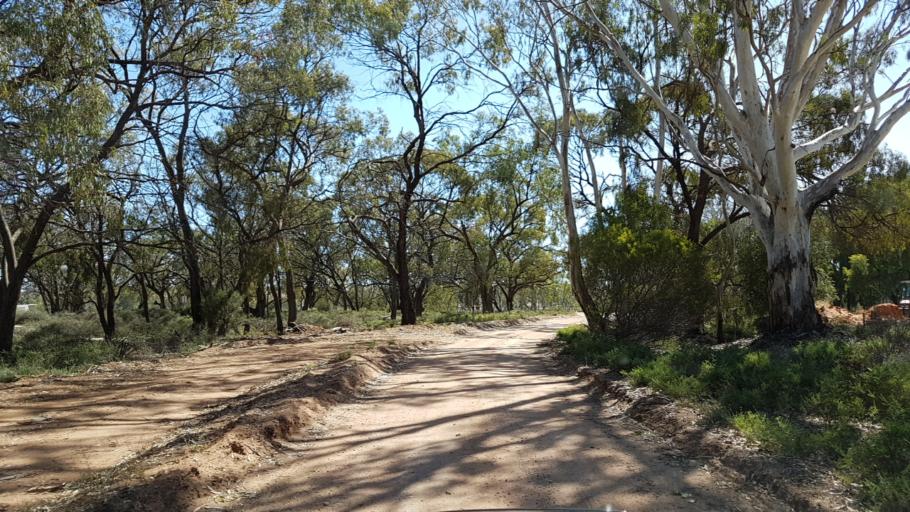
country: AU
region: South Australia
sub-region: Loxton Waikerie
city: Waikerie
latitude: -34.1634
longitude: 140.0328
